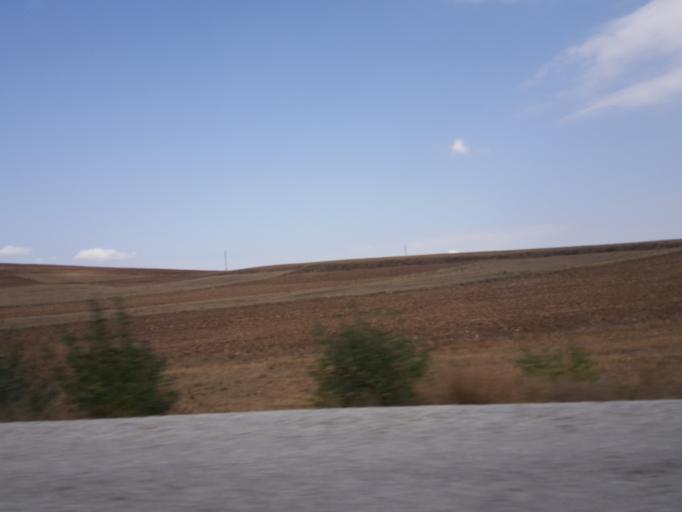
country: TR
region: Corum
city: Alaca
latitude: 40.1574
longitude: 34.7189
